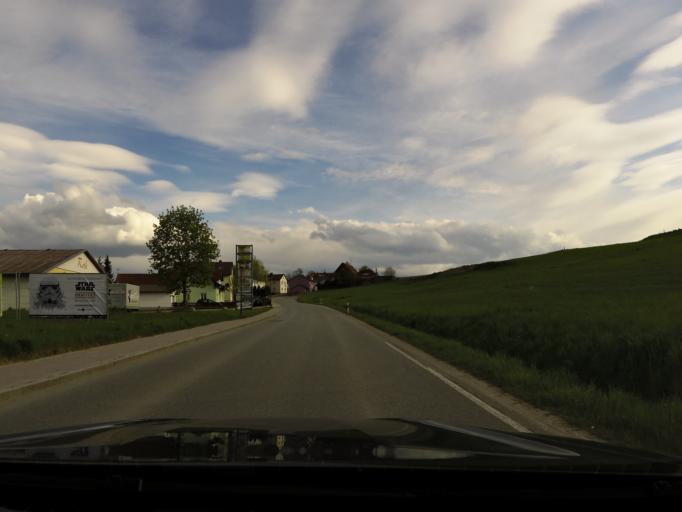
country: DE
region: Bavaria
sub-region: Upper Bavaria
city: Wang
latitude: 48.4970
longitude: 11.9227
